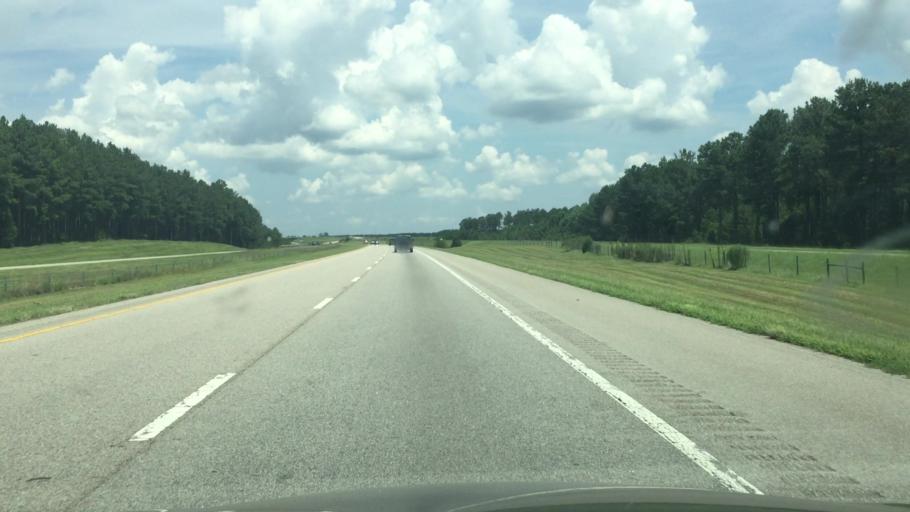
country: US
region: North Carolina
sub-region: Richmond County
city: Ellerbe
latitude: 35.1329
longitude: -79.7145
